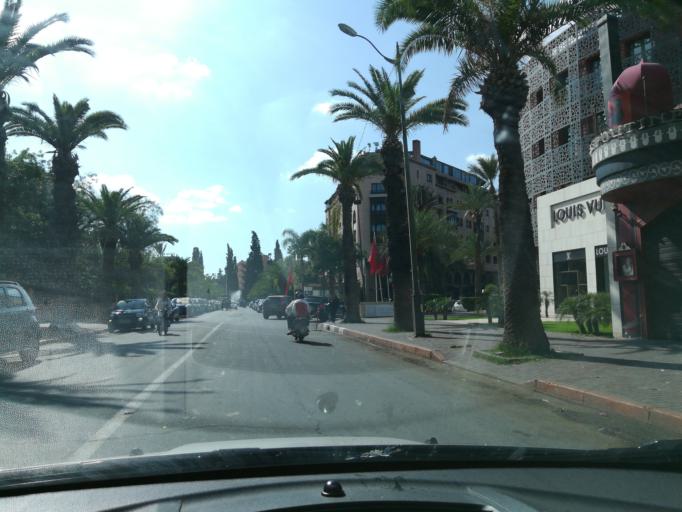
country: MA
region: Marrakech-Tensift-Al Haouz
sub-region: Marrakech
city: Marrakesh
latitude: 31.6219
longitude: -8.0003
